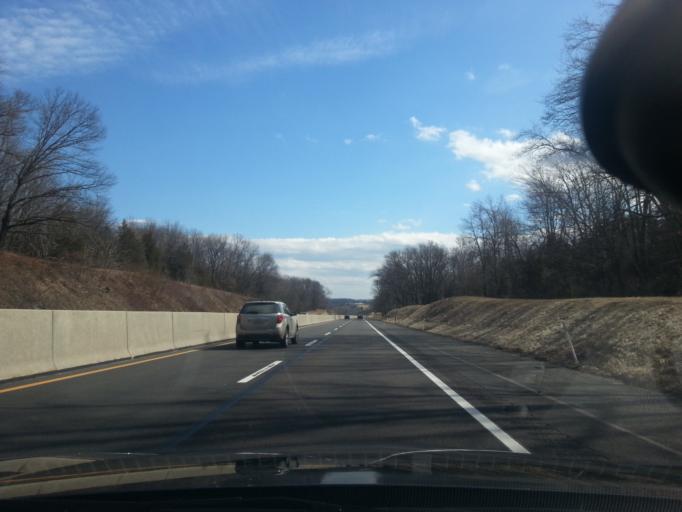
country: US
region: Pennsylvania
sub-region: Montgomery County
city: Telford
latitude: 40.3435
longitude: -75.3870
